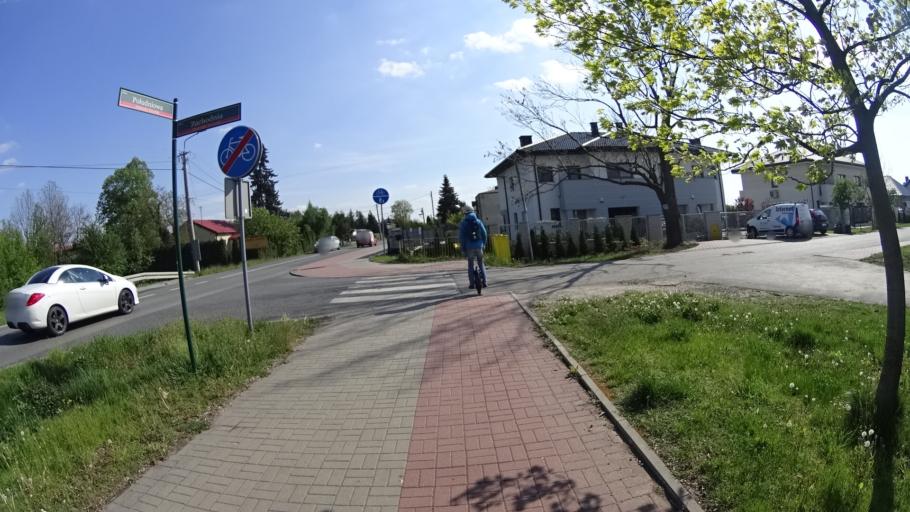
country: PL
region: Masovian Voivodeship
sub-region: Powiat warszawski zachodni
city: Stare Babice
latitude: 52.2436
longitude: 20.8186
